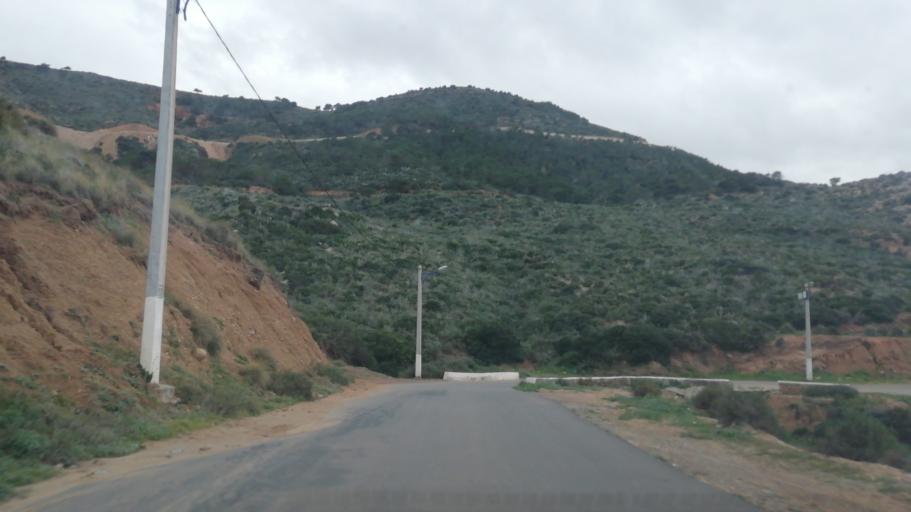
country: DZ
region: Oran
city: Bir el Djir
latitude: 35.7680
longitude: -0.5243
